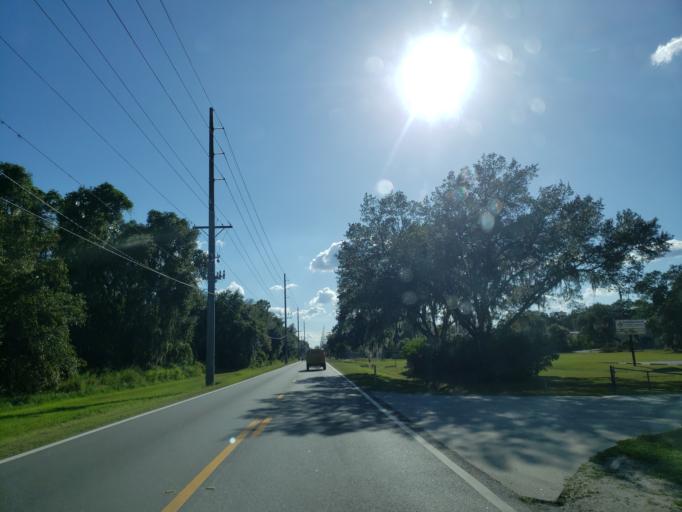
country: US
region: Florida
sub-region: Hillsborough County
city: Plant City
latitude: 28.0014
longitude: -82.1478
